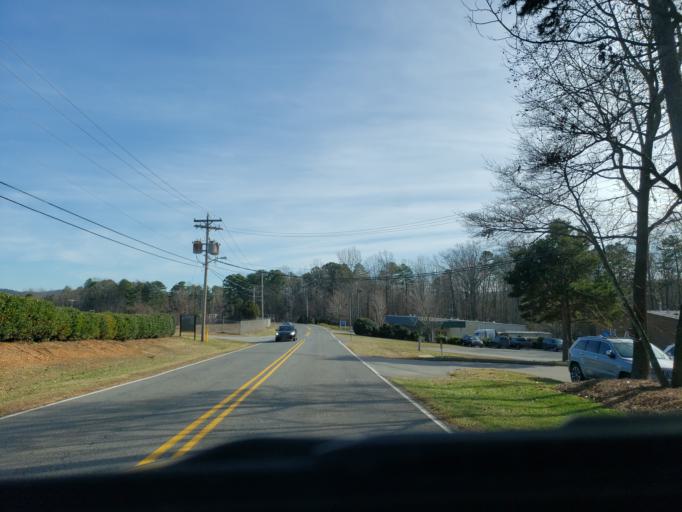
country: US
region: North Carolina
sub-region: Cleveland County
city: Kings Mountain
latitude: 35.2390
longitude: -81.3228
